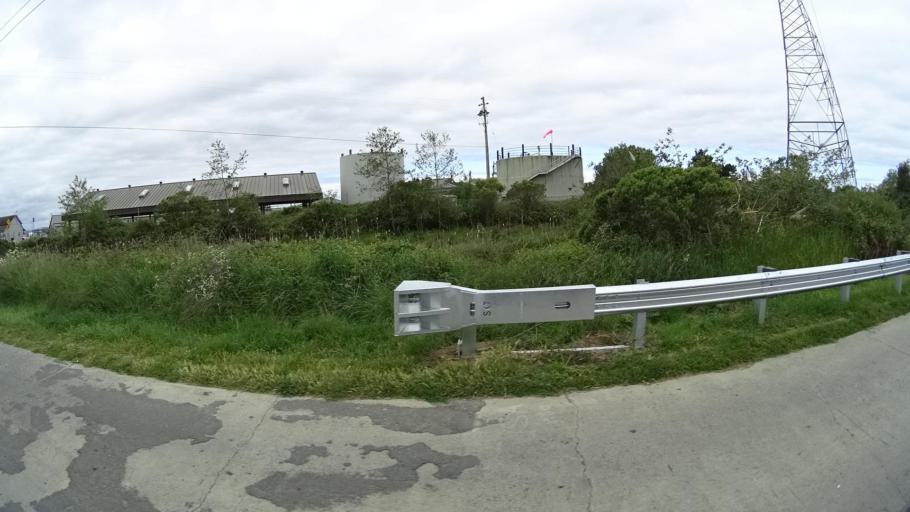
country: US
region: California
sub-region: Humboldt County
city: Arcata
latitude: 40.8560
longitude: -124.0893
